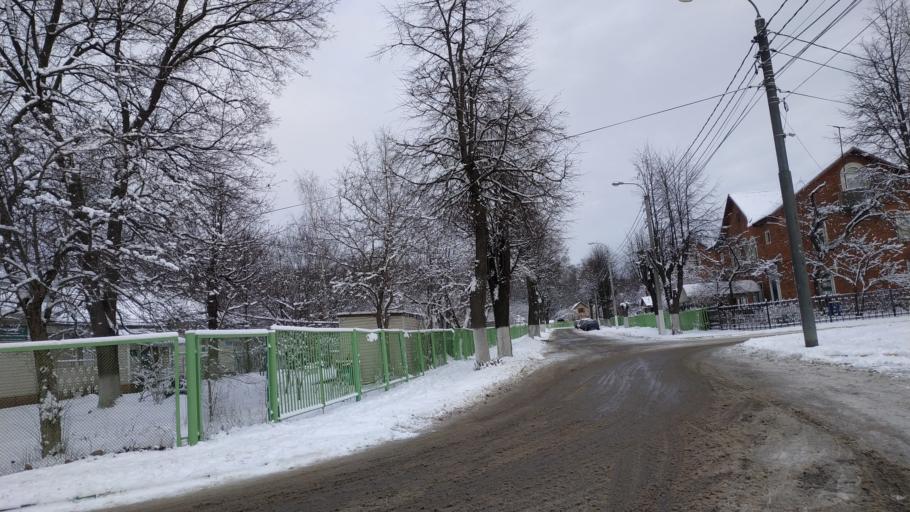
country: RU
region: Moskovskaya
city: Vidnoye
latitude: 55.5592
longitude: 37.7122
